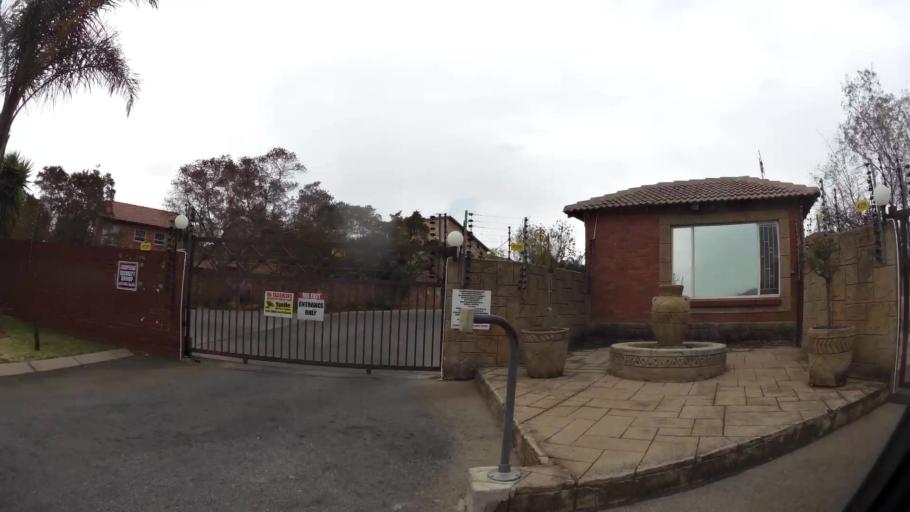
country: ZA
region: Gauteng
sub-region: City of Johannesburg Metropolitan Municipality
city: Roodepoort
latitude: -26.1069
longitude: 27.9039
